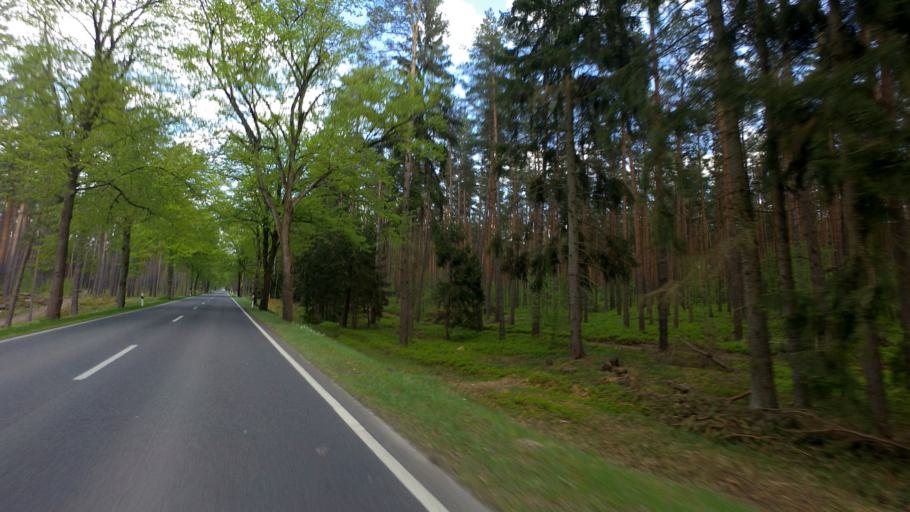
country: DE
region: Brandenburg
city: Marienwerder
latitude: 52.9471
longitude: 13.5604
